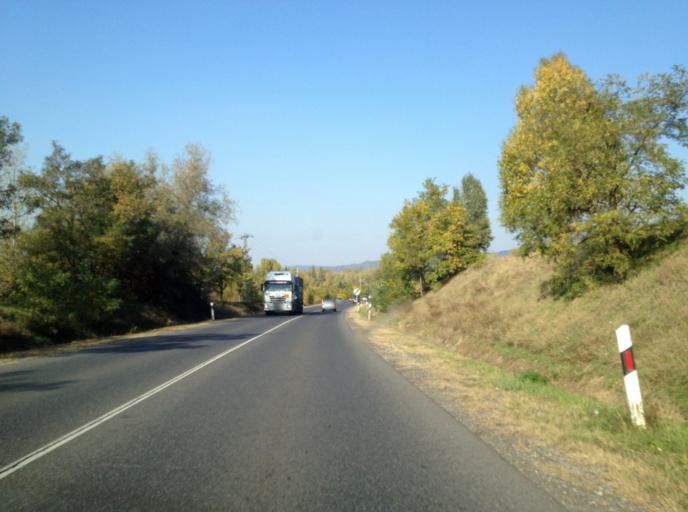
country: HU
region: Komarom-Esztergom
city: Dorog
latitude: 47.7513
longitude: 18.7382
